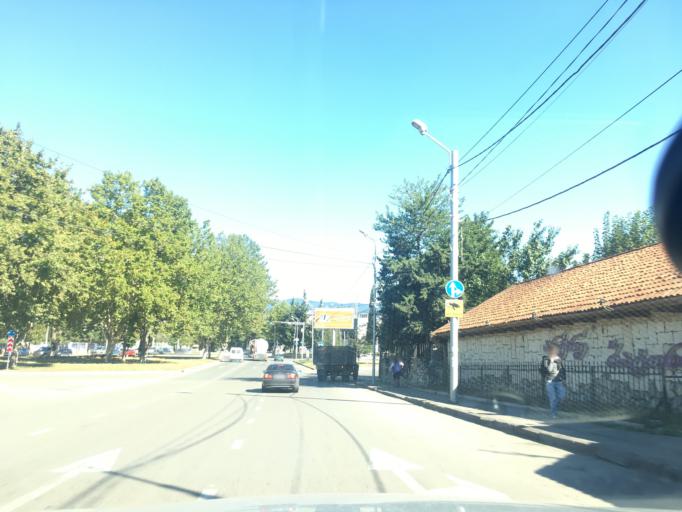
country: GE
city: Zahesi
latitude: 41.7873
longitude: 44.8008
